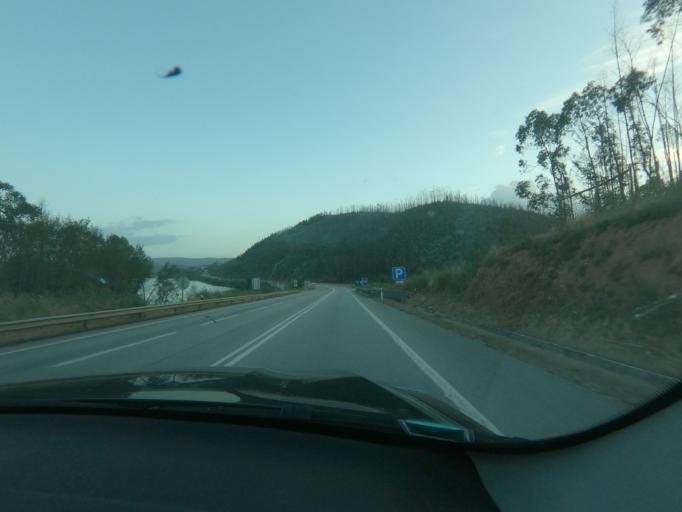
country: PT
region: Viseu
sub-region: Mortagua
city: Mortagua
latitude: 40.3356
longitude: -8.2262
